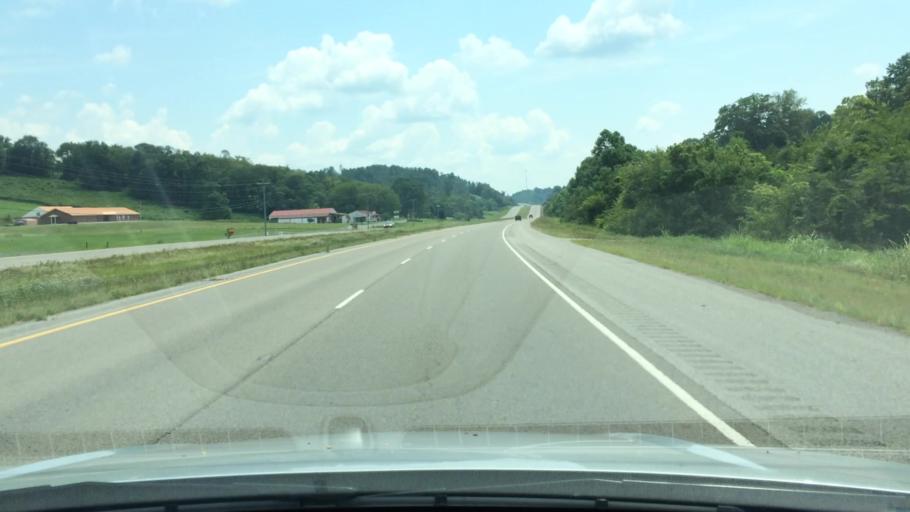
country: US
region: Tennessee
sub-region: Giles County
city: Pulaski
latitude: 35.1777
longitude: -86.9806
